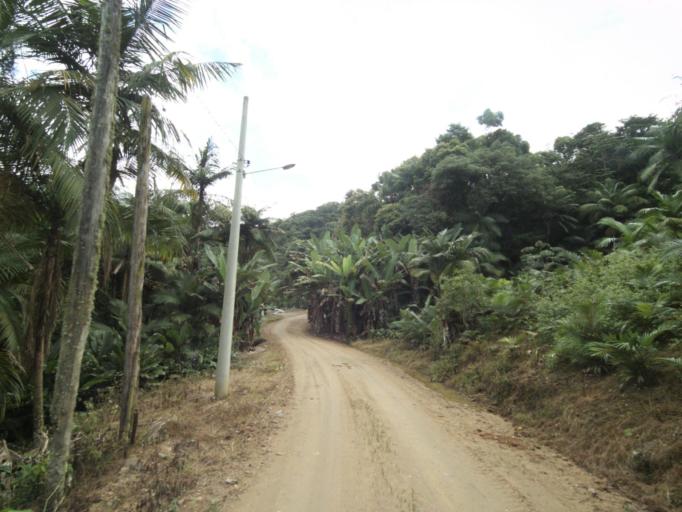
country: BR
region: Santa Catarina
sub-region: Pomerode
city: Pomerode
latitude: -26.7002
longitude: -49.2272
